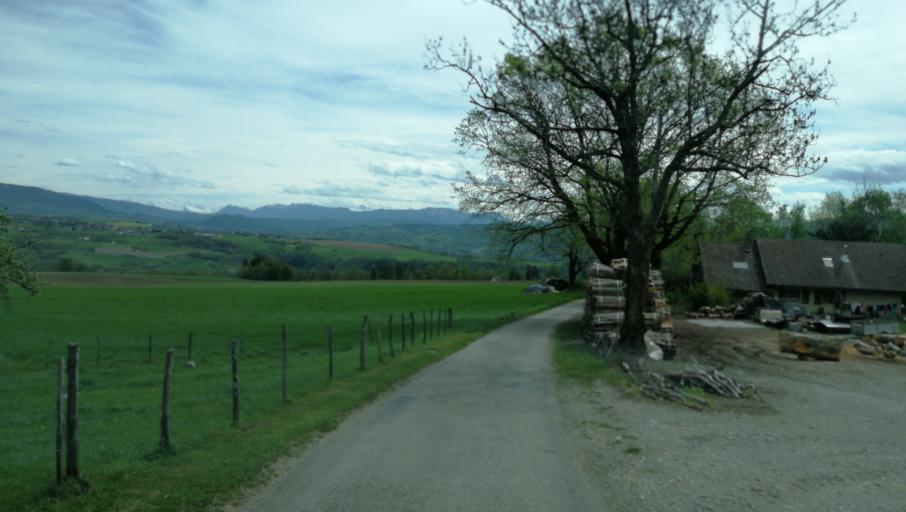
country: FR
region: Rhone-Alpes
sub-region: Departement de l'Ain
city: Bellegarde-sur-Valserine
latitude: 46.0110
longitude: 5.7781
